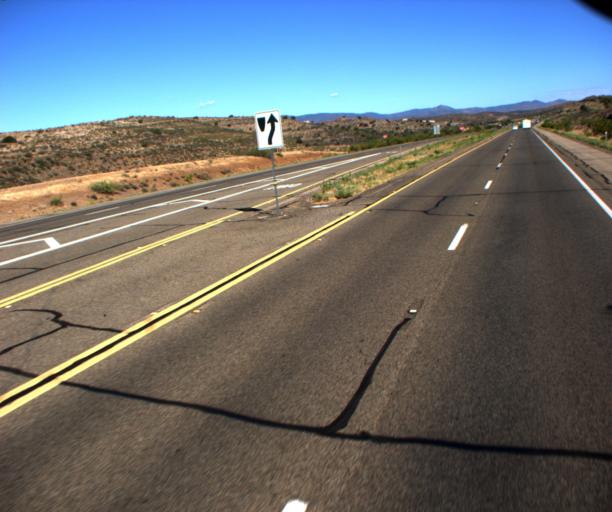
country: US
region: Arizona
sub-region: Yavapai County
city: Spring Valley
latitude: 34.3585
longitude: -112.1696
